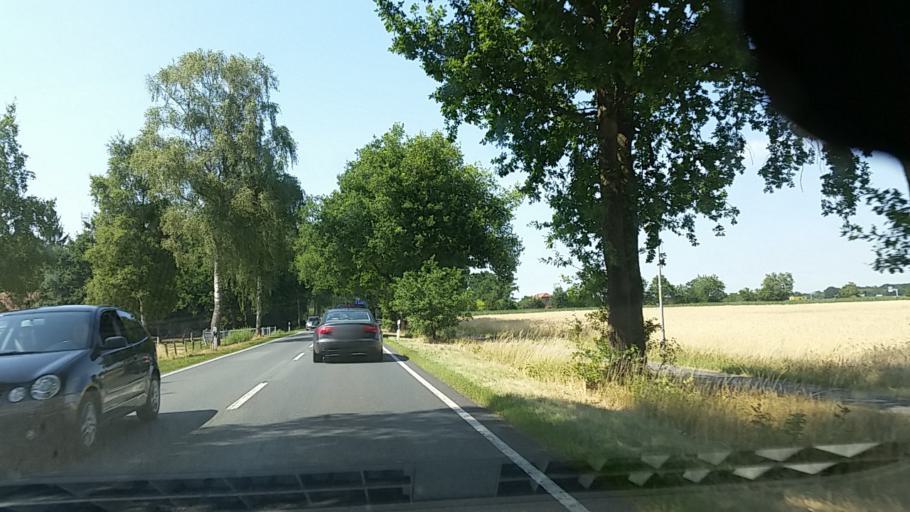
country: DE
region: Lower Saxony
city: Ottersberg
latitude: 53.0759
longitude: 9.1622
